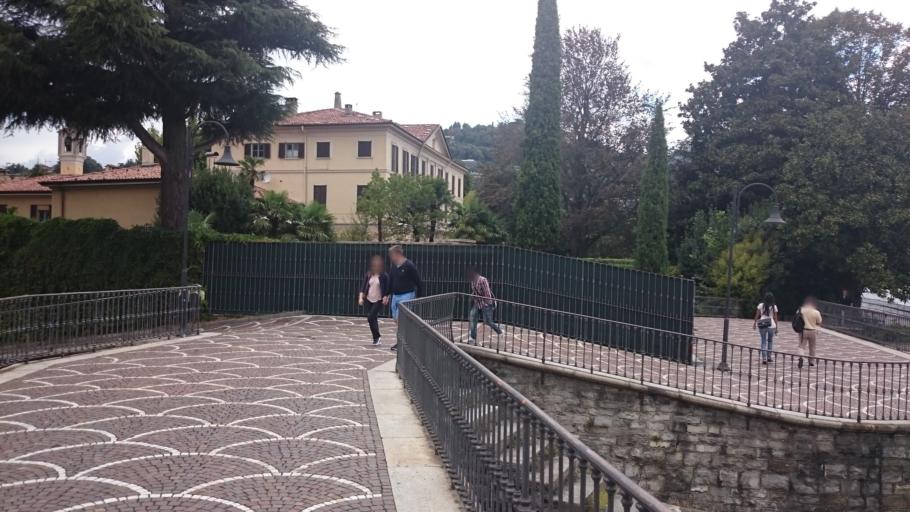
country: IT
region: Lombardy
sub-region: Provincia di Como
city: Como
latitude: 45.8155
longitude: 9.0674
